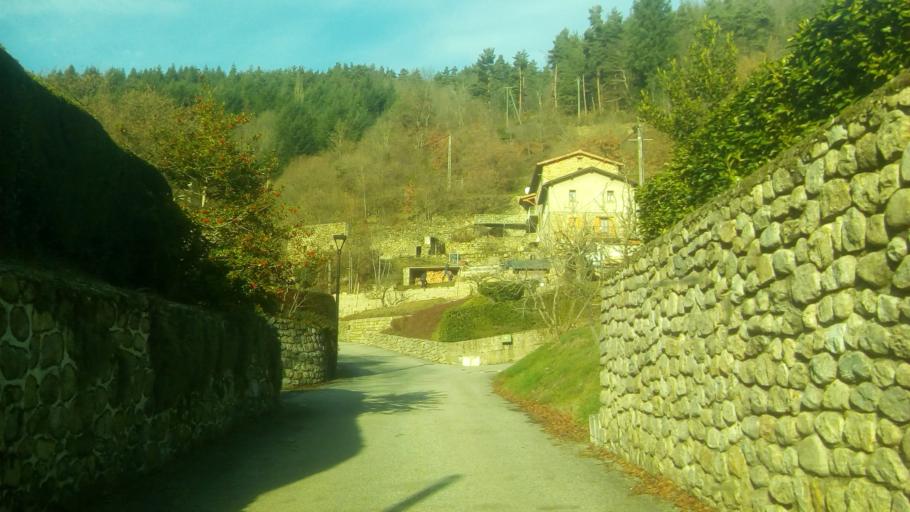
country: FR
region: Rhone-Alpes
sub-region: Departement de l'Ardeche
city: Saint-Martin-de-Valamas
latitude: 44.8831
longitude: 4.3661
